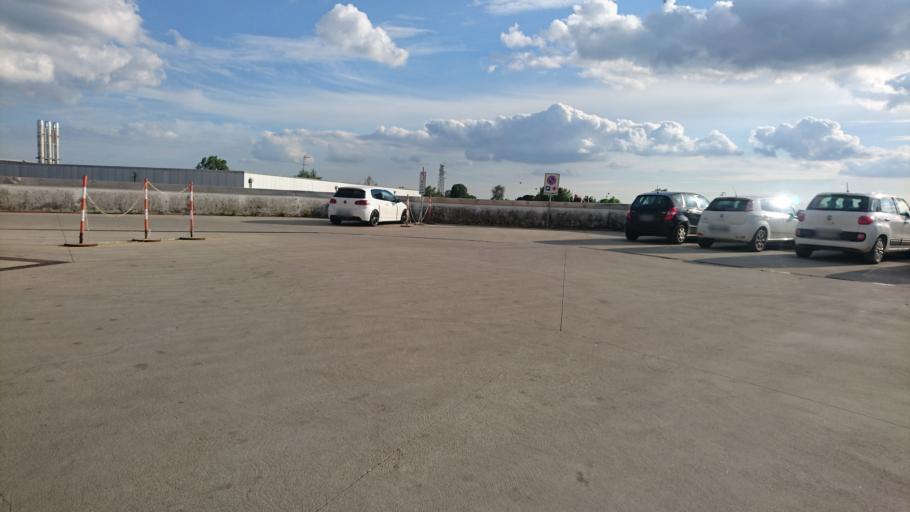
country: IT
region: Veneto
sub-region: Provincia di Rovigo
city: Trecenta
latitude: 45.0294
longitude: 11.4667
